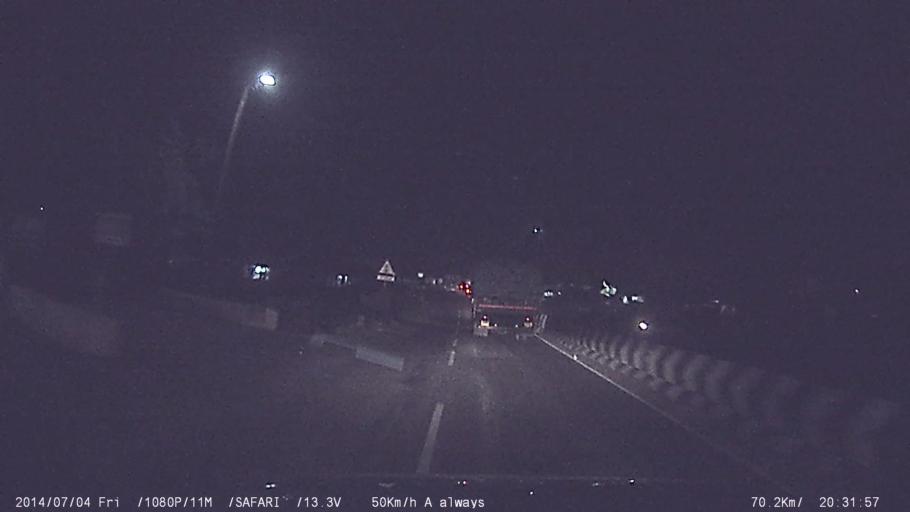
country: IN
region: Tamil Nadu
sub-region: Coimbatore
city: Madukkarai
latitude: 10.9380
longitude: 76.9516
